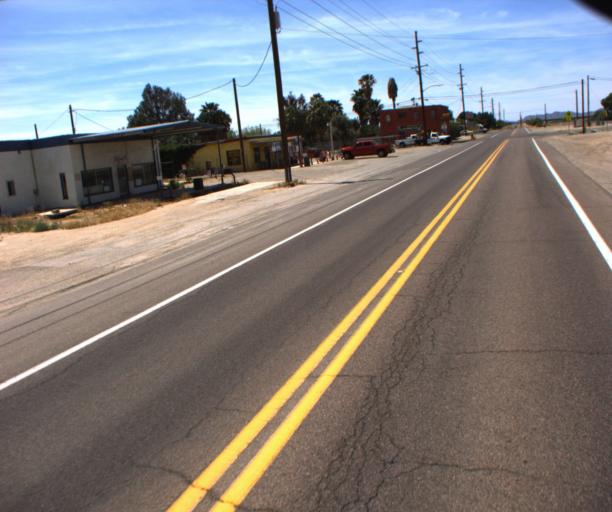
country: US
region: Arizona
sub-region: La Paz County
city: Salome
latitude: 33.8231
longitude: -113.5403
